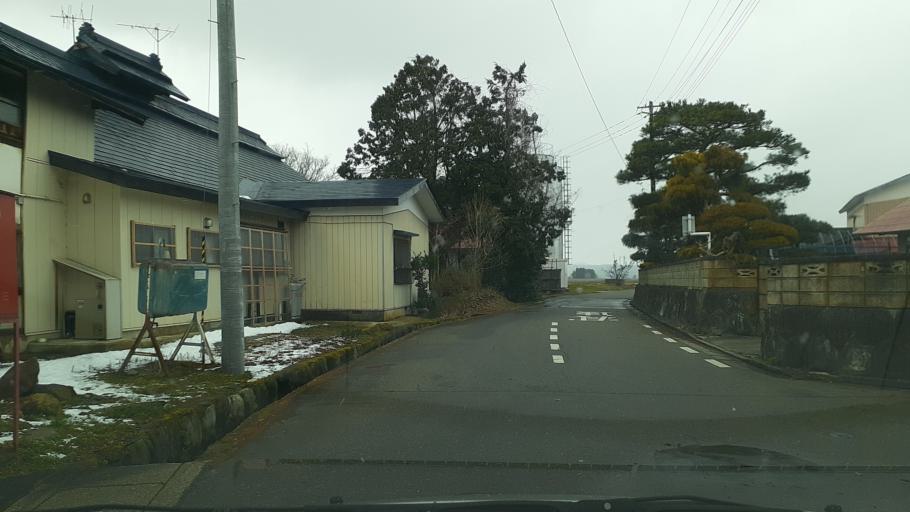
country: JP
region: Fukushima
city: Kitakata
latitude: 37.5594
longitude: 139.8844
